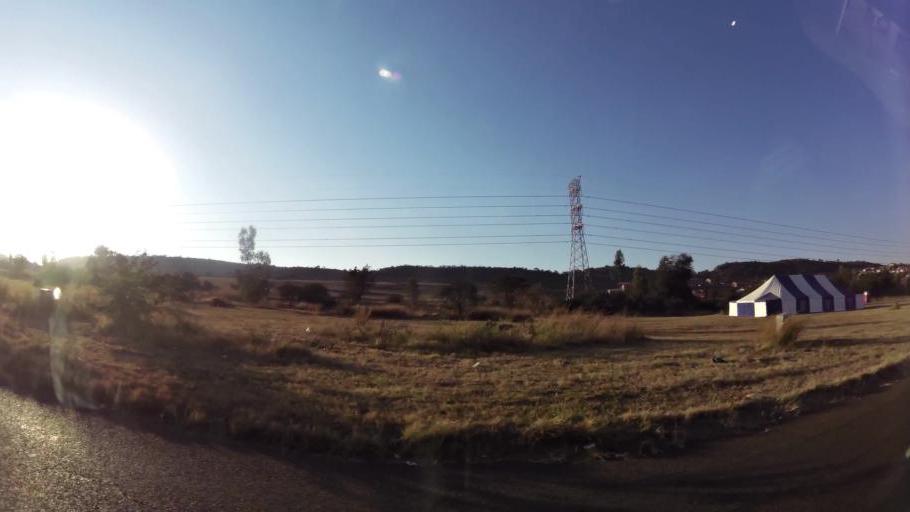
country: ZA
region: Gauteng
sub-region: City of Tshwane Metropolitan Municipality
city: Pretoria
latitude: -25.7368
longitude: 28.1149
